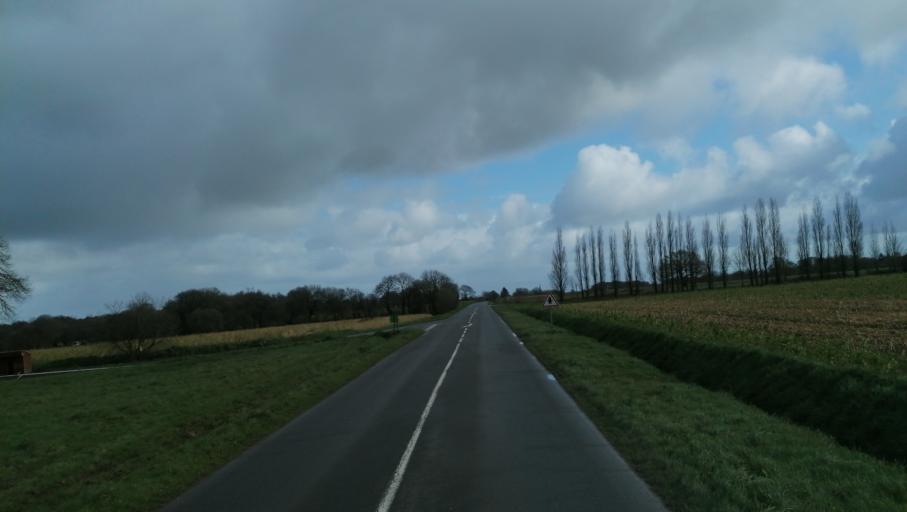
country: FR
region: Brittany
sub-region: Departement des Cotes-d'Armor
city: Lanrodec
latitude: 48.5228
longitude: -3.0244
